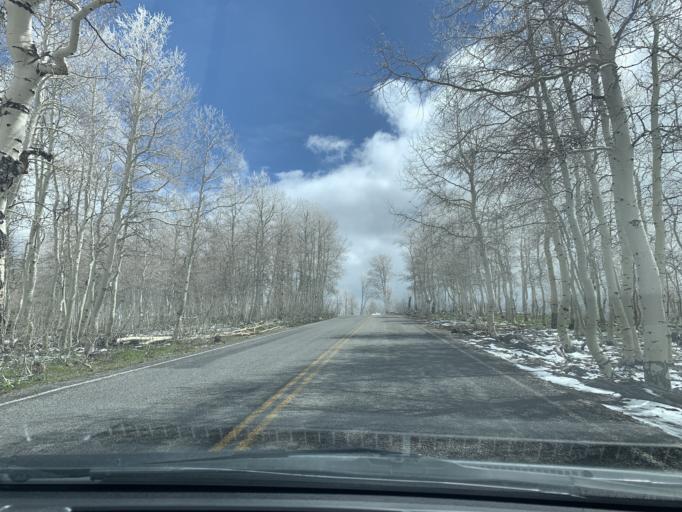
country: US
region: Utah
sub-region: Juab County
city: Mona
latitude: 39.8459
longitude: -111.7150
